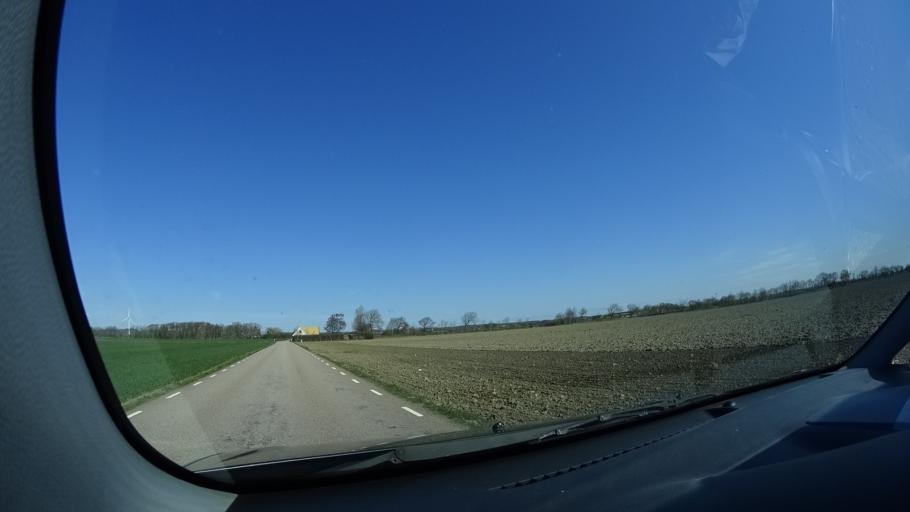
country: SE
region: Skane
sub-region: Hoganas Kommun
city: Hoganas
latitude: 56.2180
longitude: 12.5931
